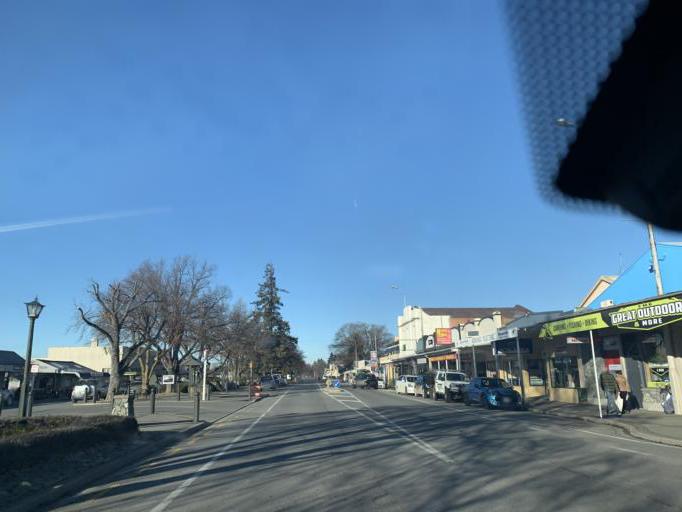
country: NZ
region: Canterbury
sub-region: Timaru District
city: Pleasant Point
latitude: -44.0980
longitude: 170.8289
